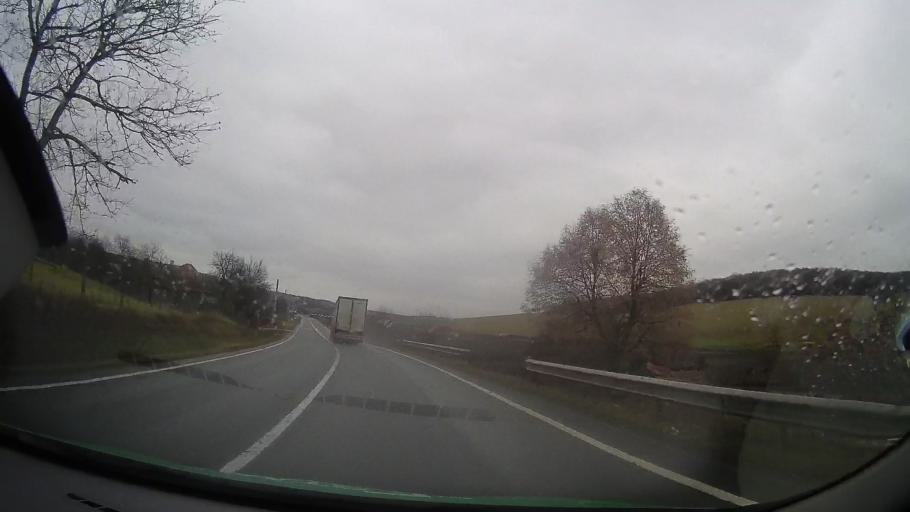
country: RO
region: Mures
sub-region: Comuna Lunca
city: Lunca
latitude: 46.8601
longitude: 24.5567
